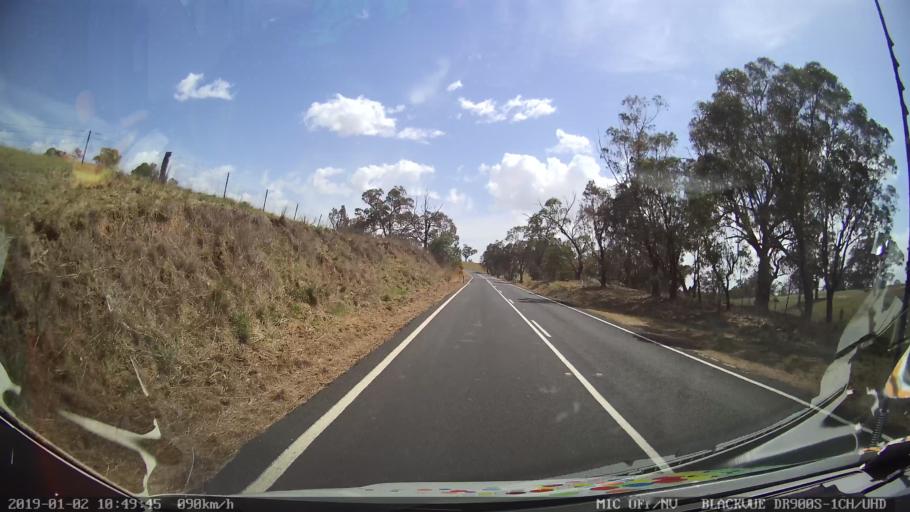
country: AU
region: New South Wales
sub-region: Cootamundra
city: Cootamundra
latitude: -34.7204
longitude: 148.2763
